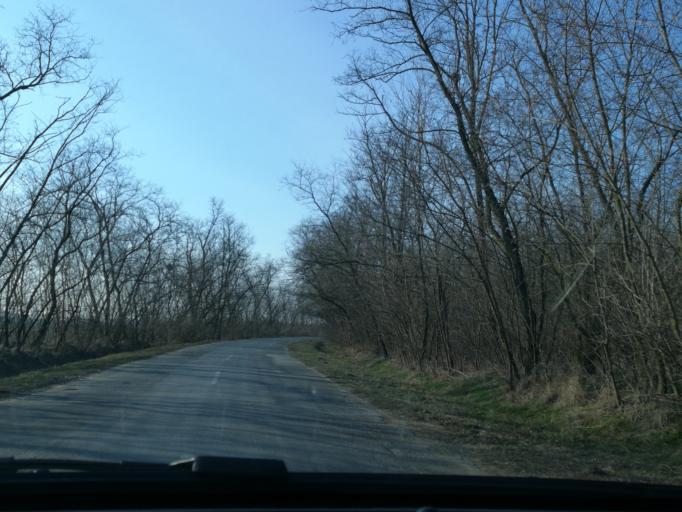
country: HU
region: Szabolcs-Szatmar-Bereg
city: Levelek
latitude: 48.0342
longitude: 21.9730
